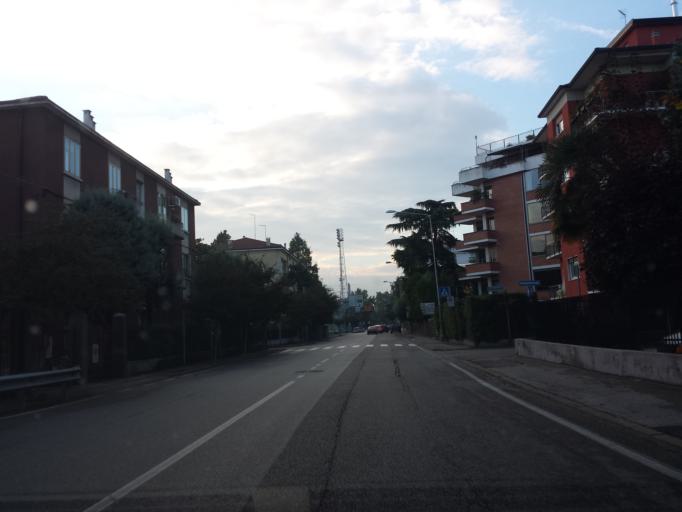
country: IT
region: Veneto
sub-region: Provincia di Vicenza
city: Vicenza
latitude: 45.5442
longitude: 11.5591
